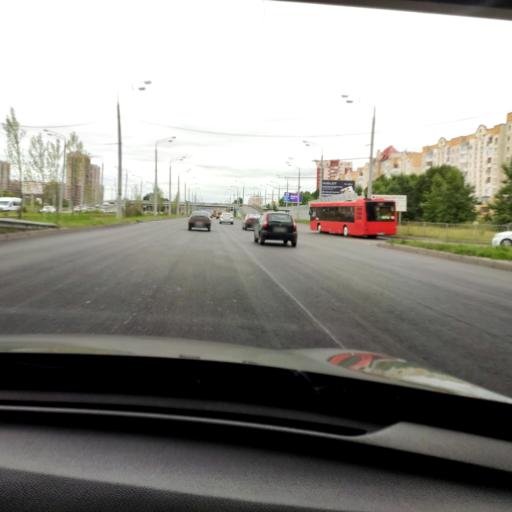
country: RU
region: Tatarstan
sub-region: Gorod Kazan'
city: Kazan
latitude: 55.7845
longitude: 49.2144
